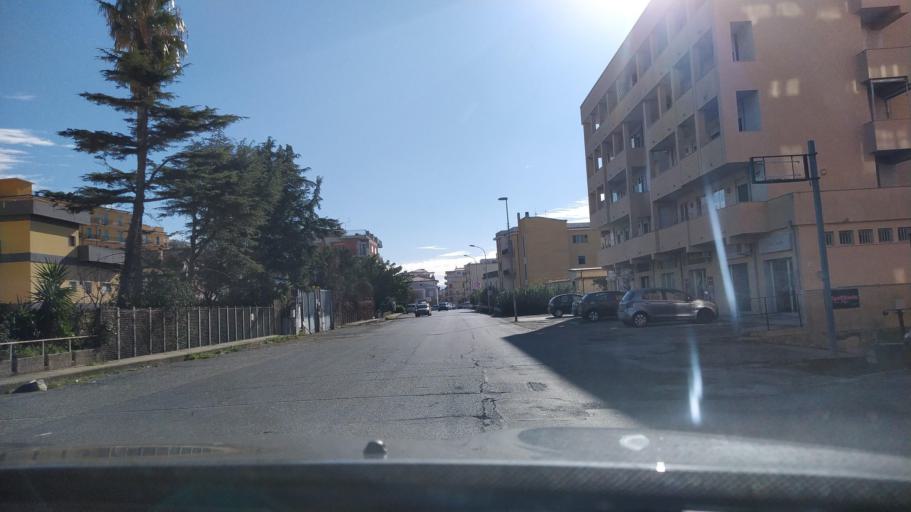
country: IT
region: Calabria
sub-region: Provincia di Cosenza
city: Paola
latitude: 39.3699
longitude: 16.0282
